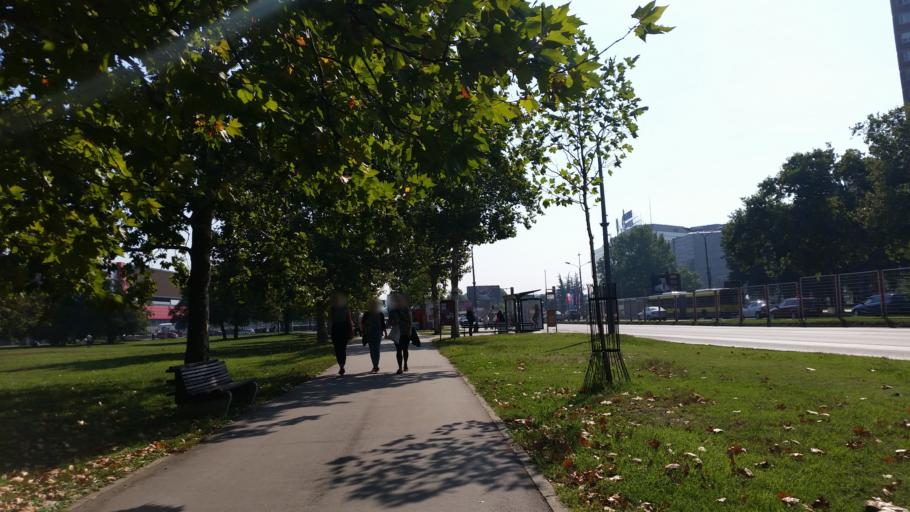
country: RS
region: Central Serbia
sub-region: Belgrade
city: Novi Beograd
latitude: 44.8155
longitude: 20.4330
